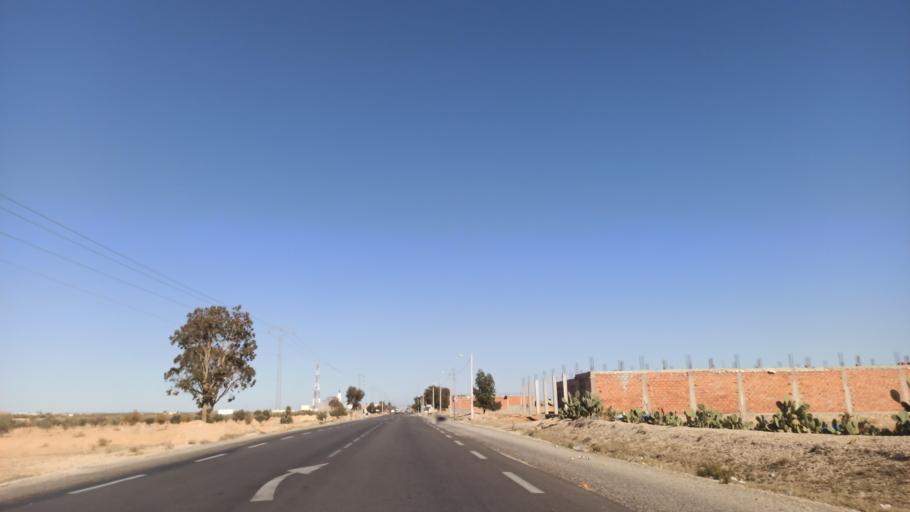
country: TN
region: Sidi Bu Zayd
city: Bi'r al Hufayy
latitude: 34.7387
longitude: 9.0721
